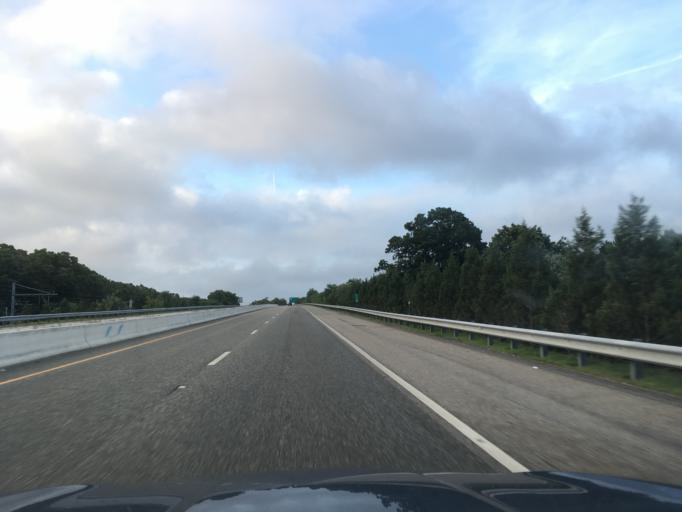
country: US
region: Rhode Island
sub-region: Kent County
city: East Greenwich
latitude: 41.6160
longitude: -71.4729
